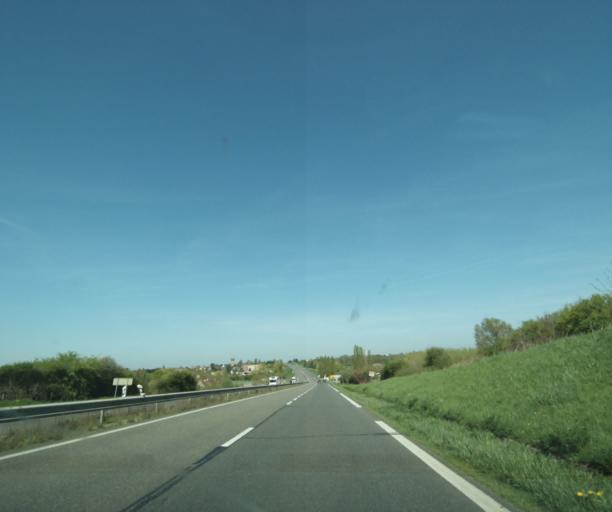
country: FR
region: Bourgogne
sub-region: Departement de la Nievre
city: Saint-Pierre-le-Moutier
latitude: 46.7874
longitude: 3.1264
